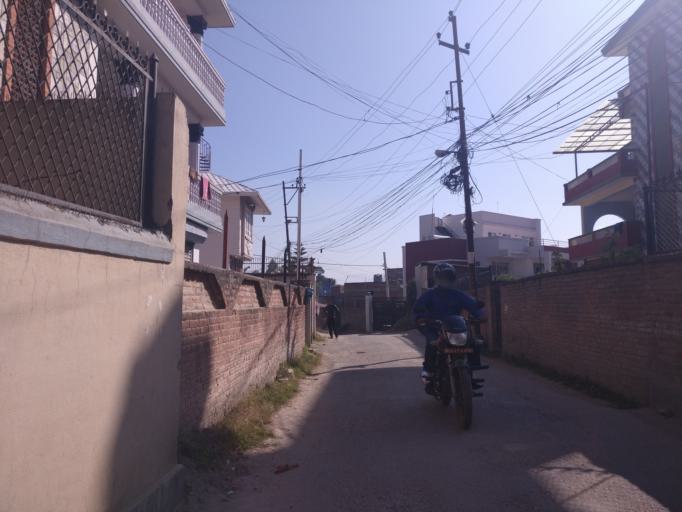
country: NP
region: Central Region
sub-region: Bagmati Zone
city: Patan
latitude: 27.6491
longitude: 85.3057
